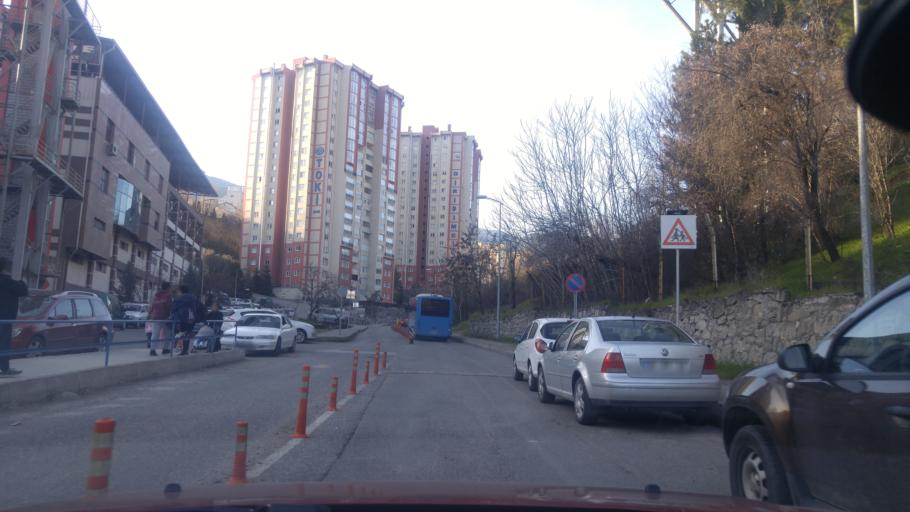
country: TR
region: Karabuk
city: Karabuk
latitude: 41.1991
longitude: 32.6163
